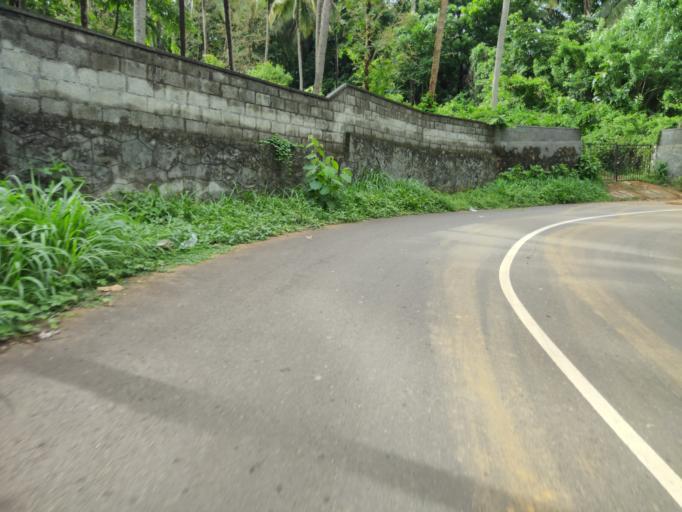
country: IN
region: Kerala
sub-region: Malappuram
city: Manjeri
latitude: 11.1381
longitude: 76.1304
